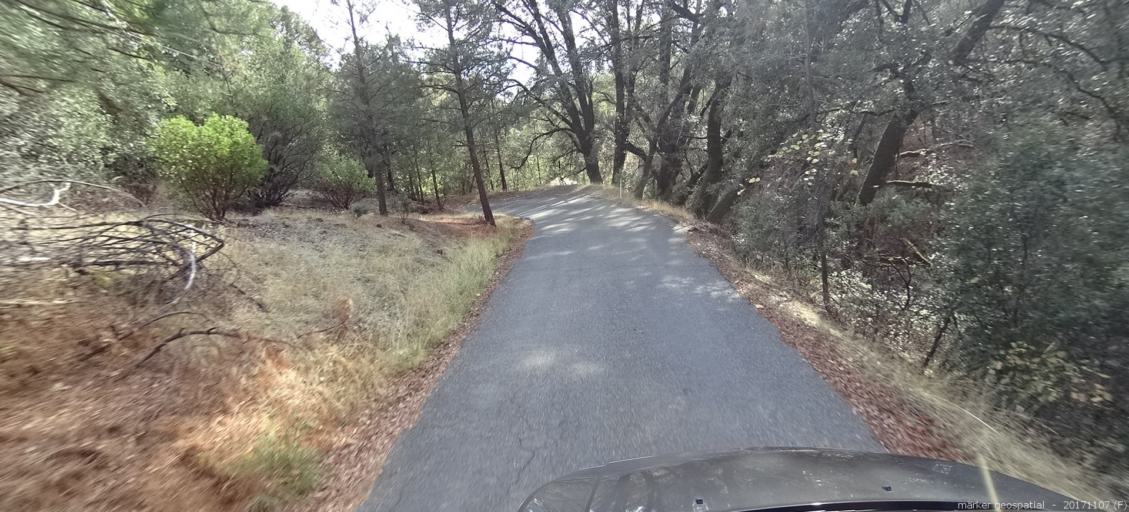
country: US
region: California
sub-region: Shasta County
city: Shasta
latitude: 40.5419
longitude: -122.5700
